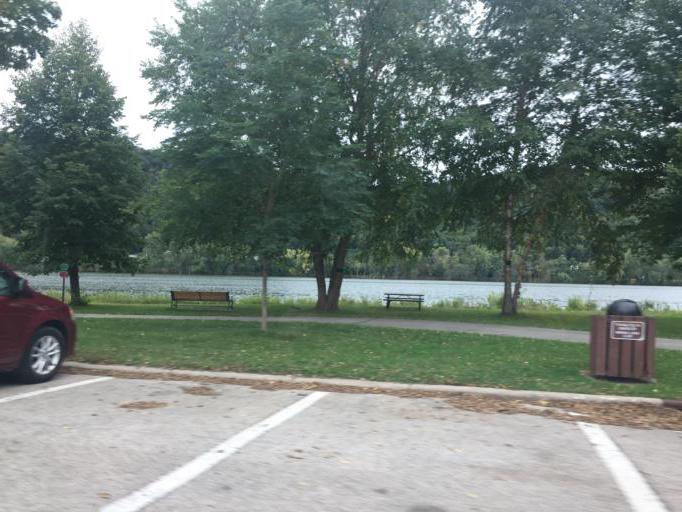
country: US
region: Minnesota
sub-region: Winona County
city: Winona
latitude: 44.0408
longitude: -91.6441
